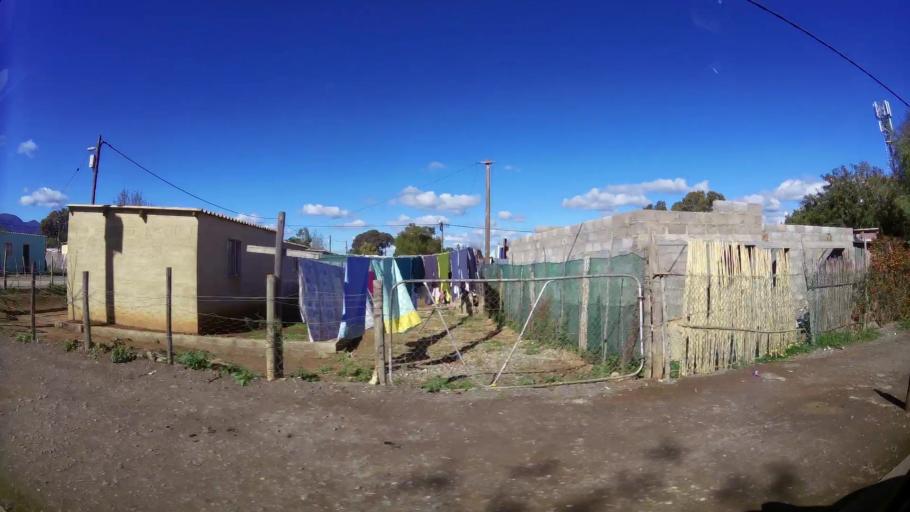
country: ZA
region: Western Cape
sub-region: Cape Winelands District Municipality
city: Ashton
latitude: -33.7928
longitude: 19.8817
